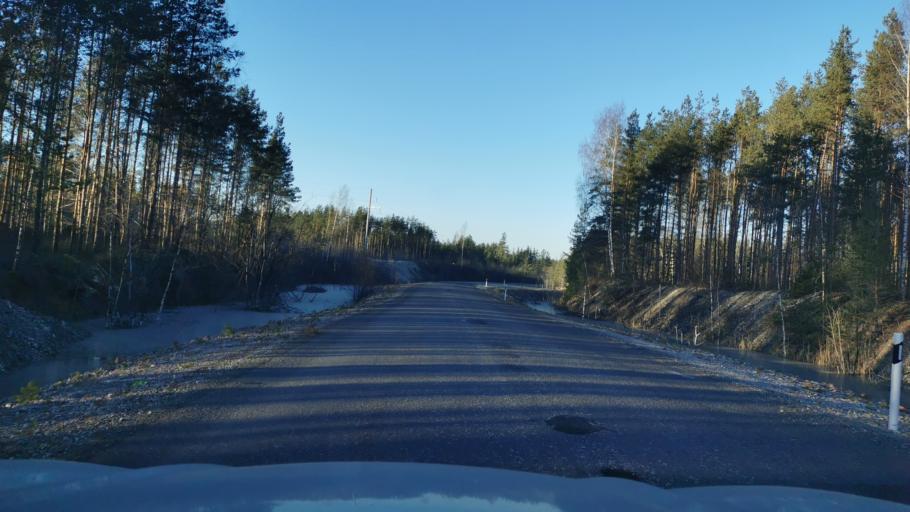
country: EE
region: Ida-Virumaa
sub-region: Puessi linn
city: Pussi
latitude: 59.3350
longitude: 27.1025
